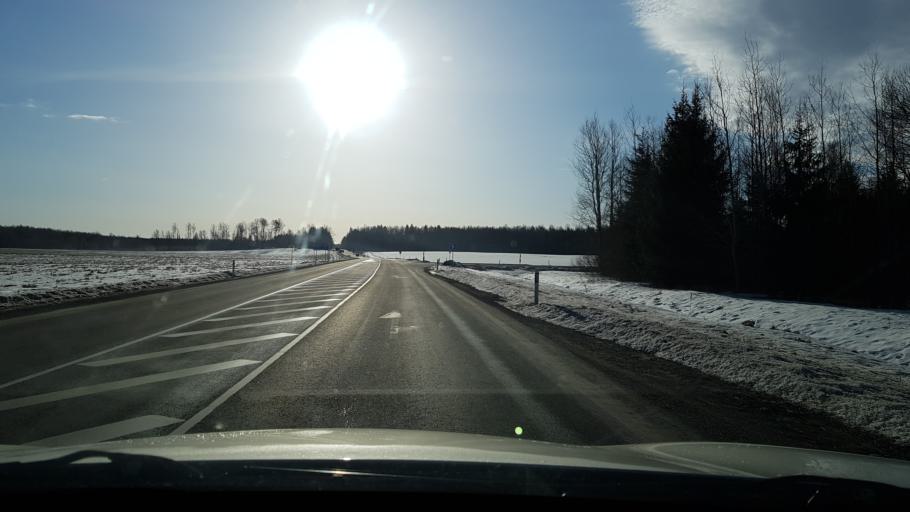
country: EE
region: Viljandimaa
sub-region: Vohma linn
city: Vohma
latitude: 58.5672
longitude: 25.5747
